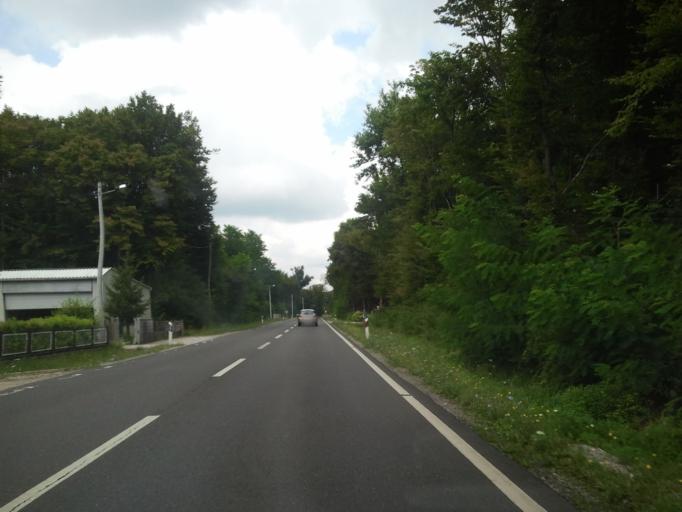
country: HR
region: Grad Zagreb
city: Horvati
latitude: 45.7181
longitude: 15.7799
